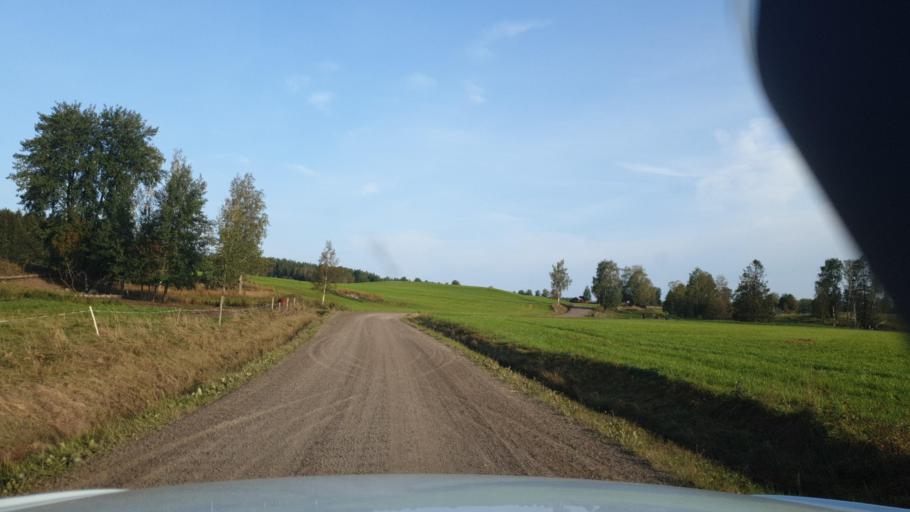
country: SE
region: Vaermland
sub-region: Eda Kommun
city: Amotfors
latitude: 59.7195
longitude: 12.1445
